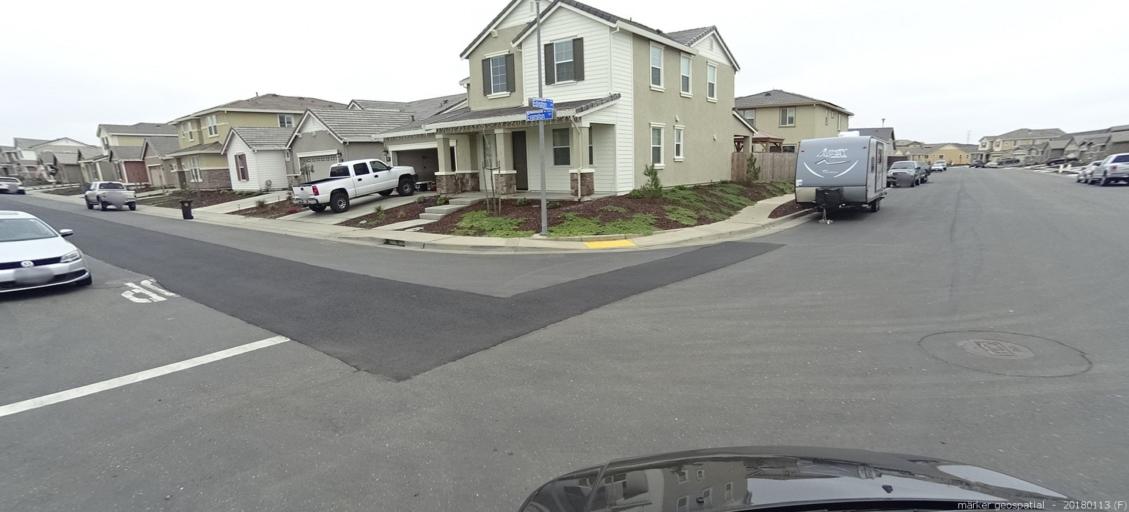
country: US
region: California
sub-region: Sacramento County
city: Gold River
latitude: 38.5730
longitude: -121.1980
